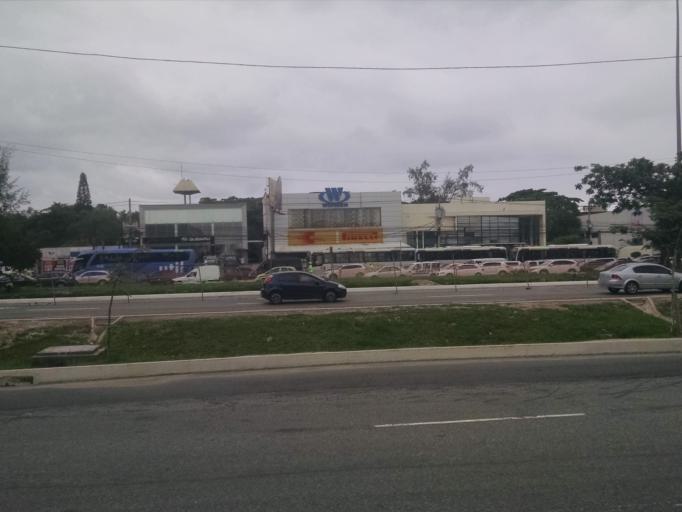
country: BR
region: Rio de Janeiro
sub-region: Rio De Janeiro
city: Rio de Janeiro
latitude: -22.9996
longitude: -43.3558
